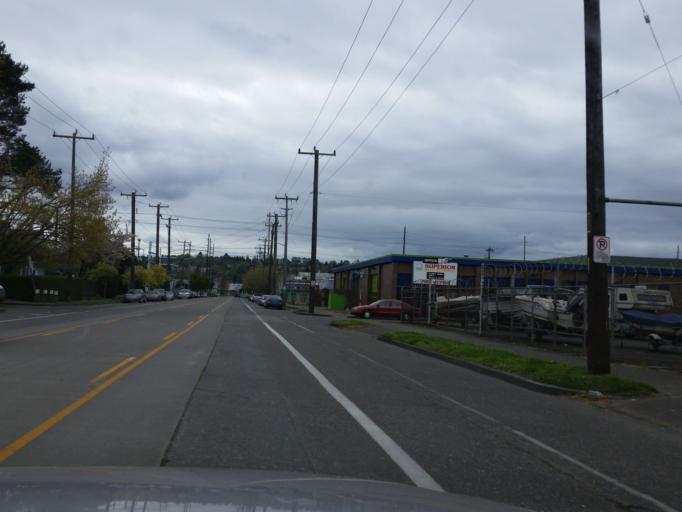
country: US
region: Washington
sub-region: King County
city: Seattle
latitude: 47.6641
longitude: -122.3663
